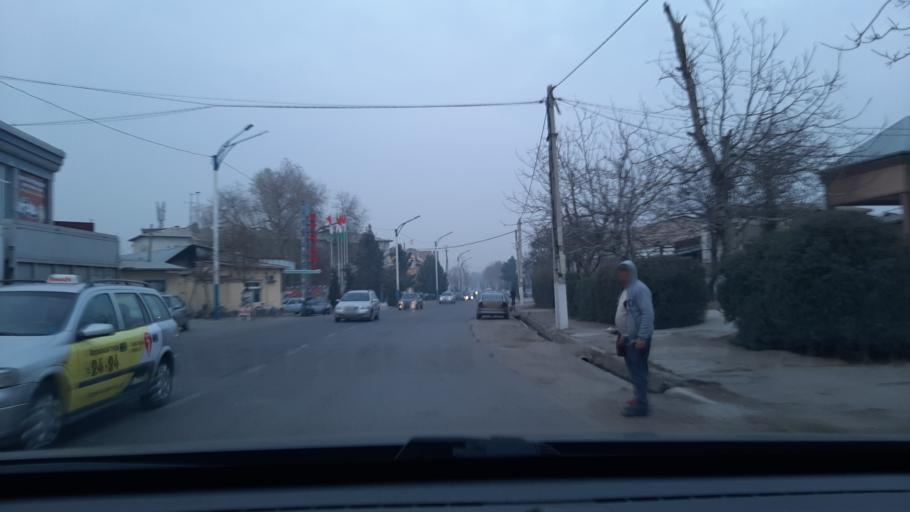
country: TJ
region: Viloyati Sughd
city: Khujand
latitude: 40.2683
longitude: 69.6019
